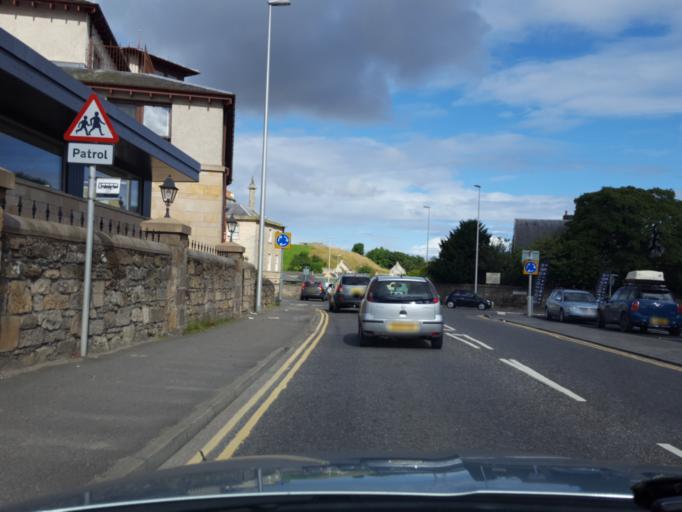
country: GB
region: Scotland
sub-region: Moray
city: Elgin
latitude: 57.6461
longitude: -3.3189
